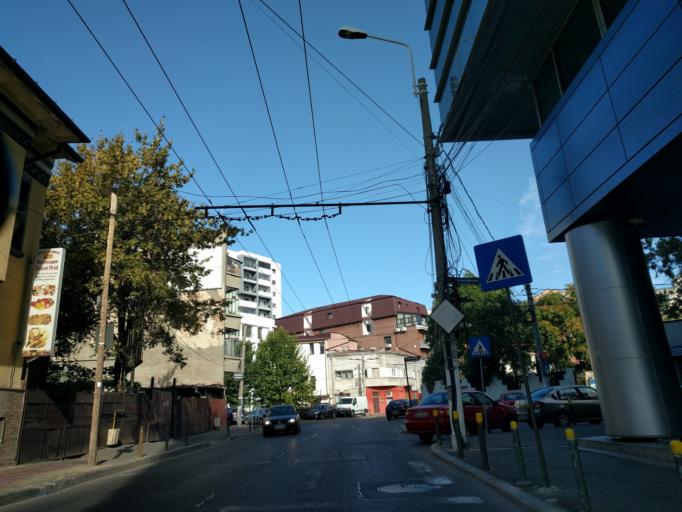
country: RO
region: Bucuresti
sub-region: Municipiul Bucuresti
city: Bucharest
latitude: 44.4296
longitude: 26.1307
